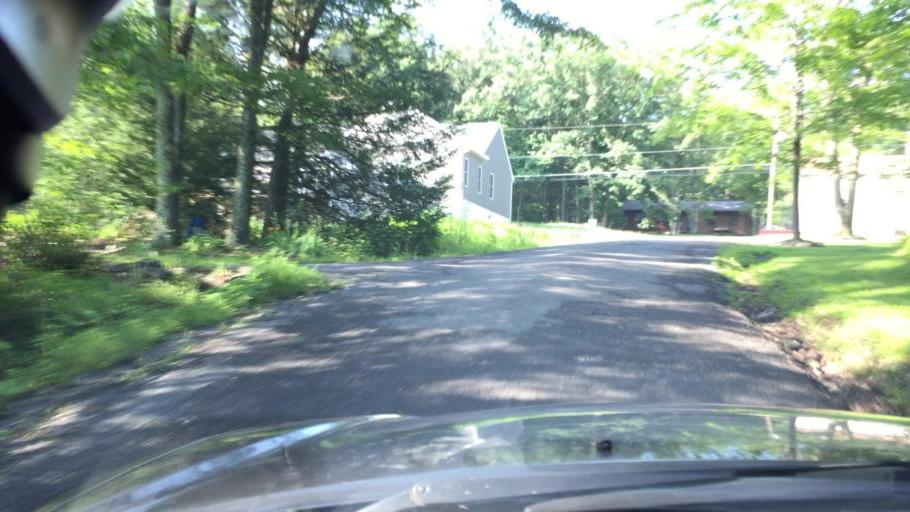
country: US
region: Pennsylvania
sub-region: Carbon County
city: Jim Thorpe
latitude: 40.8786
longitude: -75.7548
